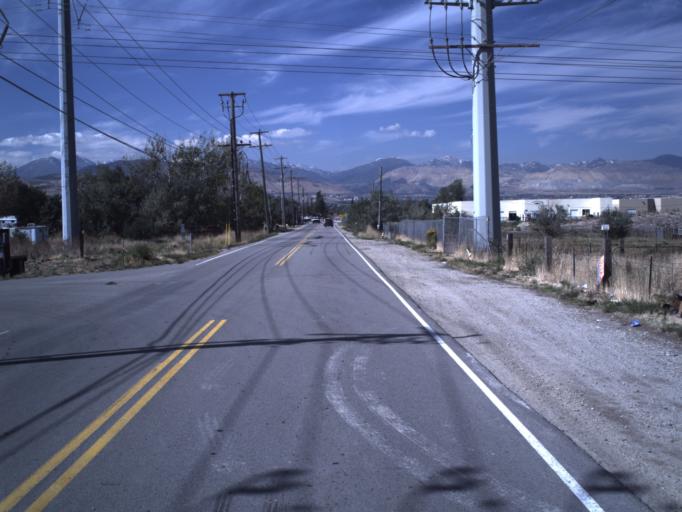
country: US
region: Utah
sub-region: Salt Lake County
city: Bluffdale
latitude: 40.4862
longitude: -111.9142
